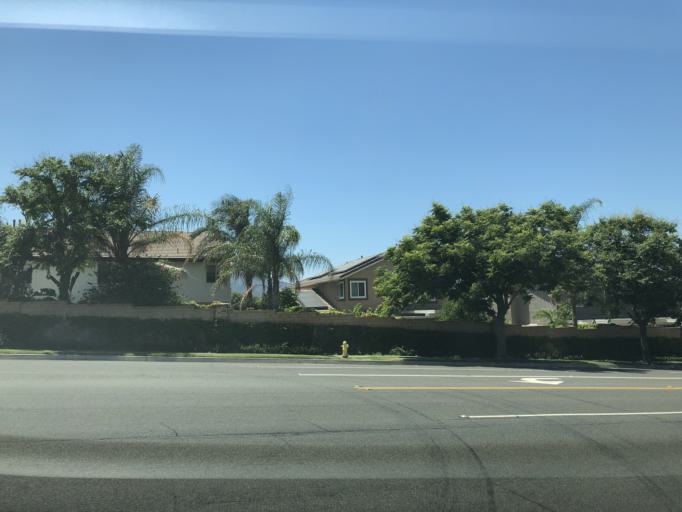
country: US
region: California
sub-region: Riverside County
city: Corona
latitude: 33.8471
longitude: -117.5791
